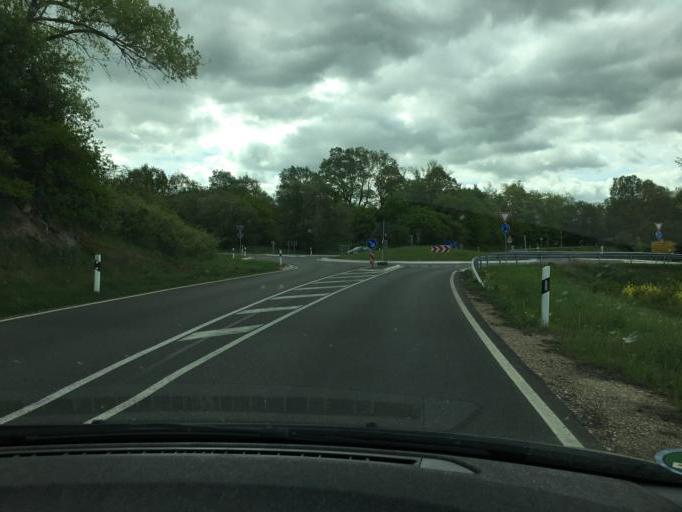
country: DE
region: North Rhine-Westphalia
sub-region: Regierungsbezirk Koln
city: Mechernich
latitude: 50.6421
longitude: 6.6558
